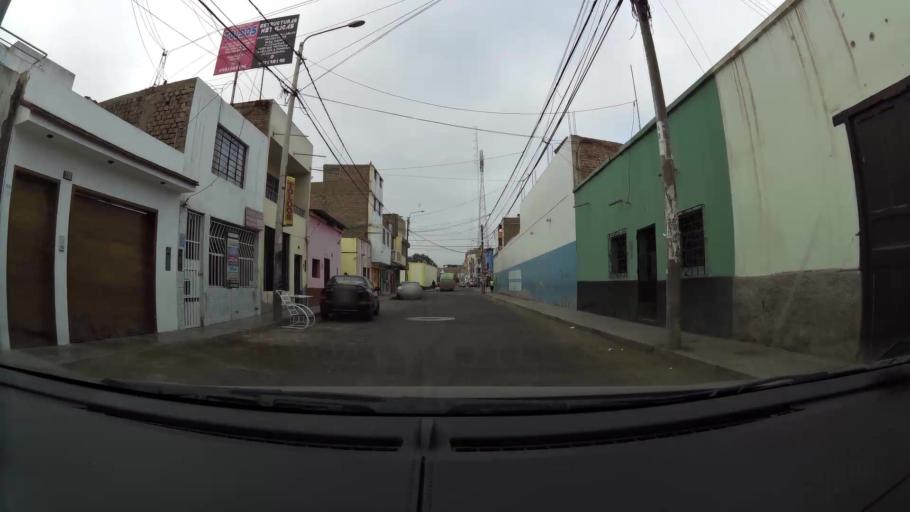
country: PE
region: La Libertad
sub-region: Provincia de Trujillo
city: Trujillo
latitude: -8.1053
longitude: -79.0289
